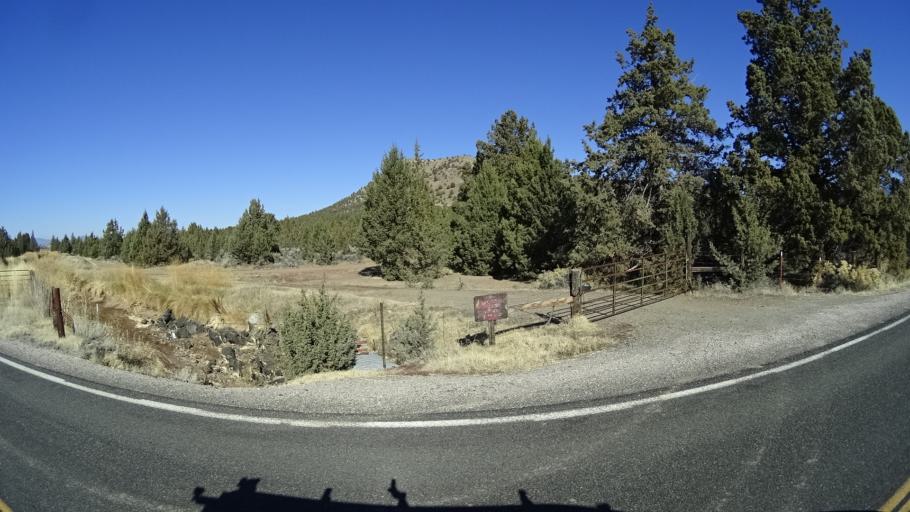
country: US
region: California
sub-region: Siskiyou County
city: Montague
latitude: 41.6598
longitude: -122.3853
